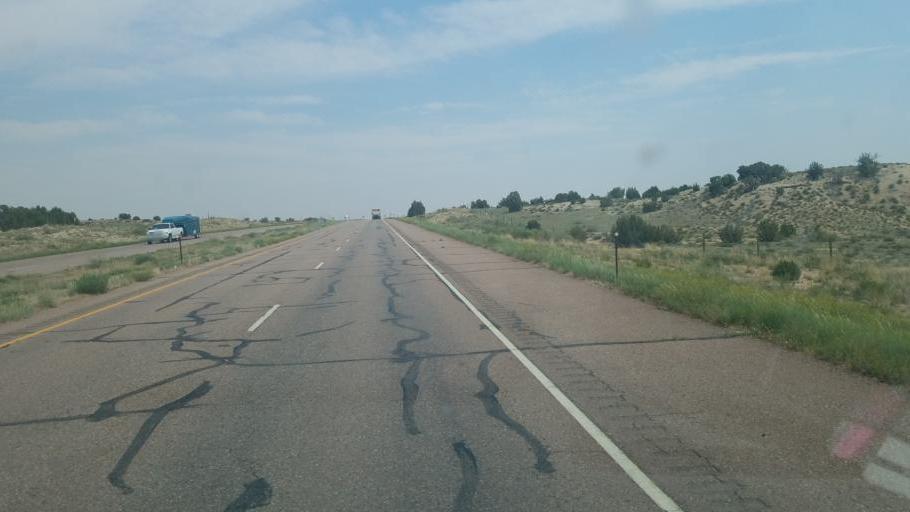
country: US
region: Colorado
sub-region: Fremont County
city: Penrose
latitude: 38.3966
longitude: -104.9754
